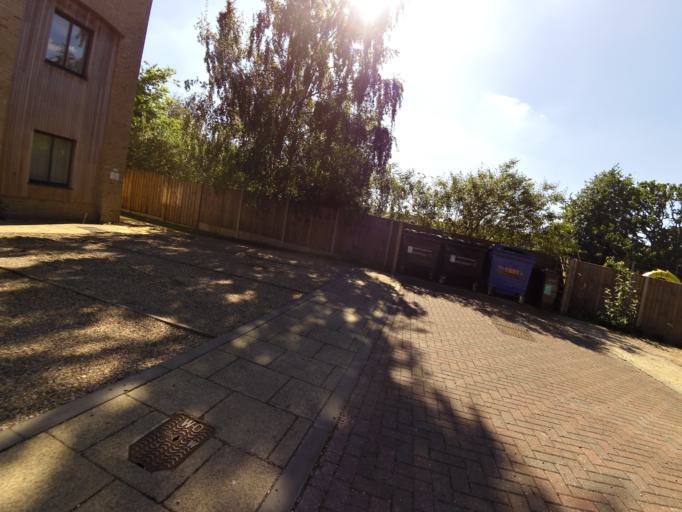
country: GB
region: England
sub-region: Norfolk
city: Thorpe Hamlet
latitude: 52.6241
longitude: 1.3232
